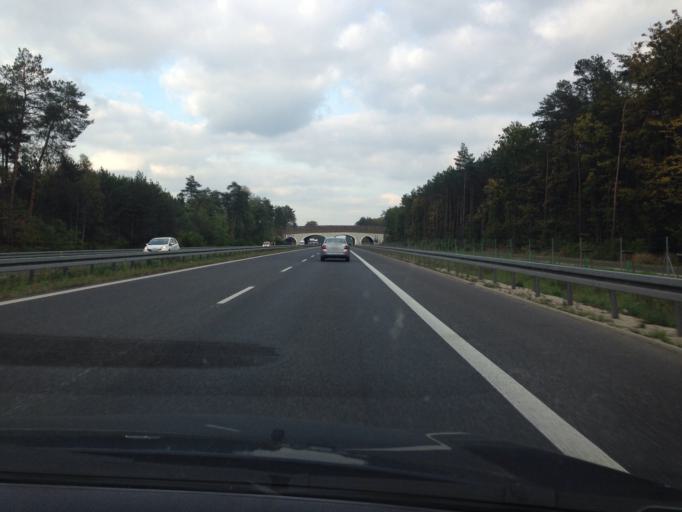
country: PL
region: Greater Poland Voivodeship
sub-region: Powiat poznanski
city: Pobiedziska
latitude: 52.4451
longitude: 17.3581
